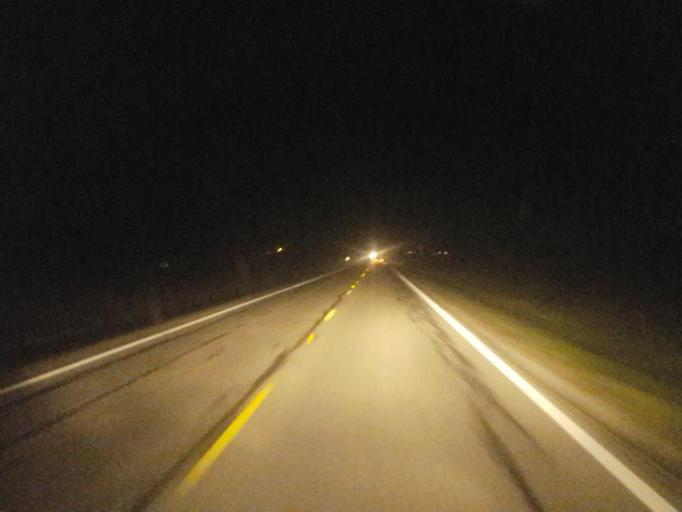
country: US
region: Ohio
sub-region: Marion County
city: Marion
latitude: 40.6145
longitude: -83.2220
